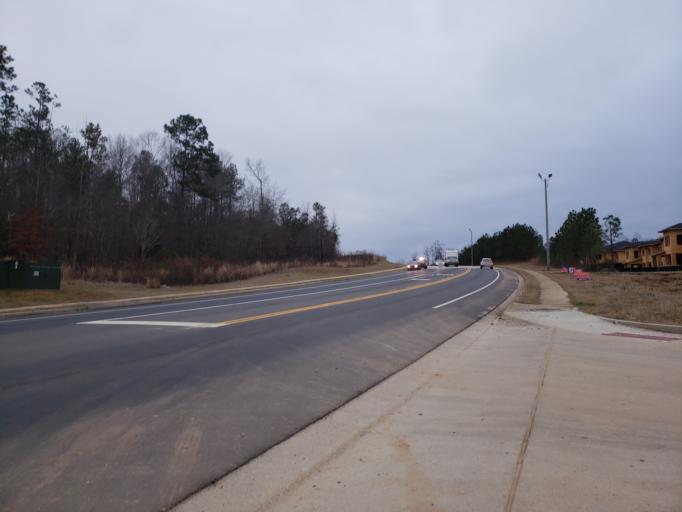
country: US
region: Alabama
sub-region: Lee County
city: Auburn
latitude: 32.5989
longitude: -85.4474
